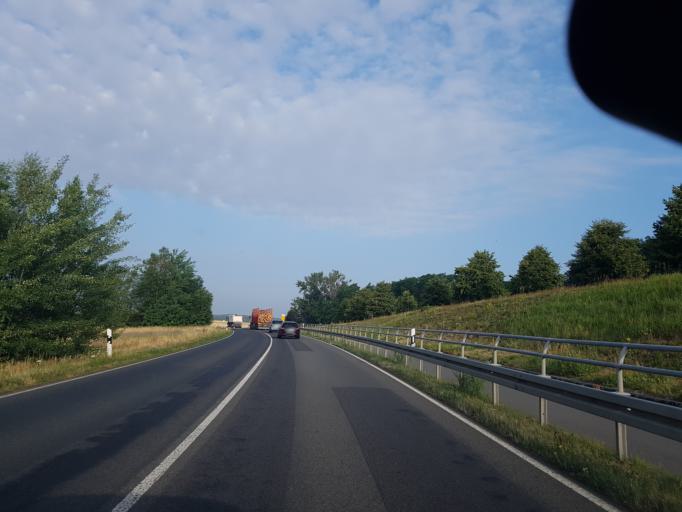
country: DE
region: Brandenburg
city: Schlieben
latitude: 51.7320
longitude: 13.3279
